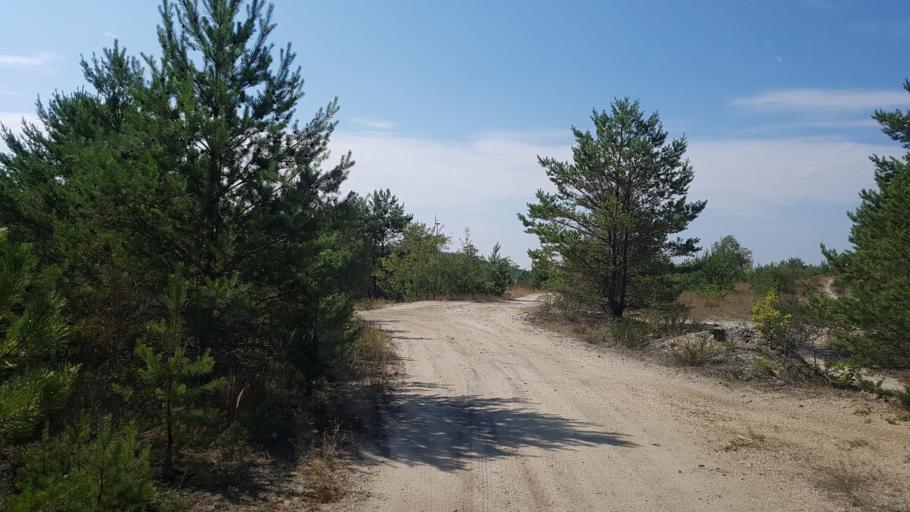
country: DE
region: Brandenburg
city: Sallgast
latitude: 51.5519
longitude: 13.8423
